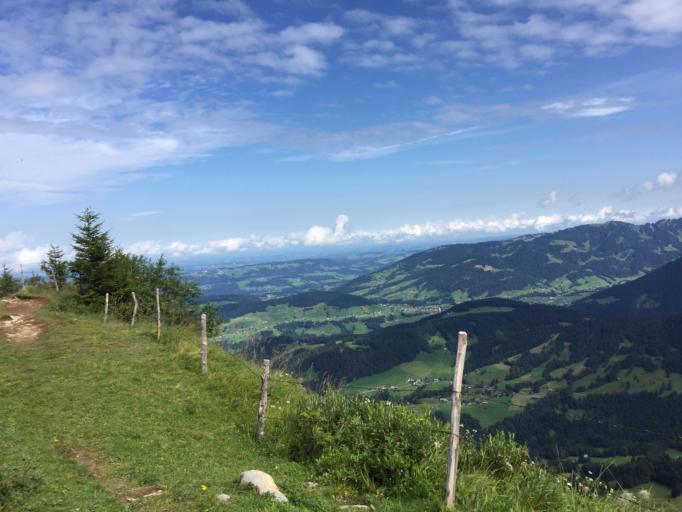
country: AT
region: Vorarlberg
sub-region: Politischer Bezirk Bregenz
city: Bizau
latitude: 47.4041
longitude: 9.9424
